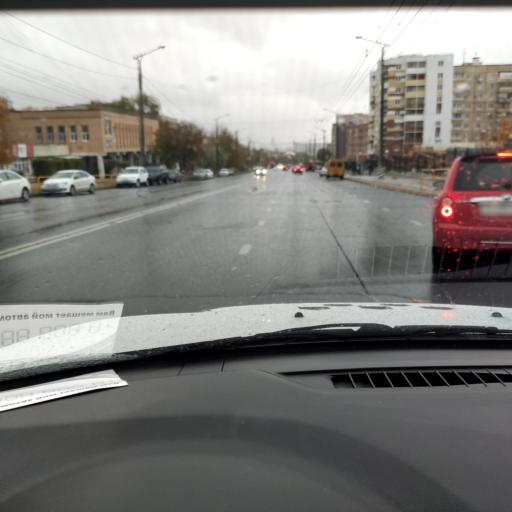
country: RU
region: Samara
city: Zhigulevsk
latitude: 53.4753
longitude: 49.4649
